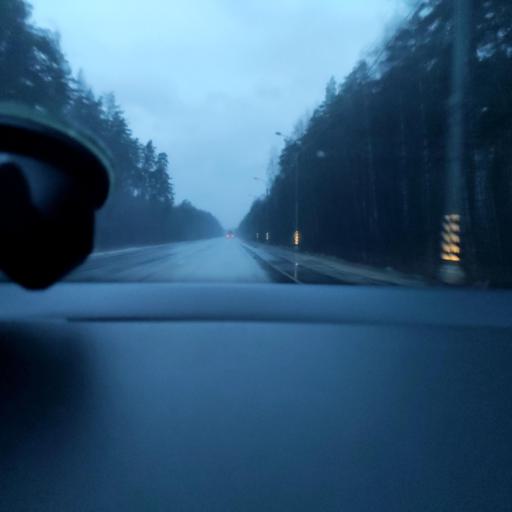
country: RU
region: Moskovskaya
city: Il'inskiy Pogost
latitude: 55.4659
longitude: 38.9723
